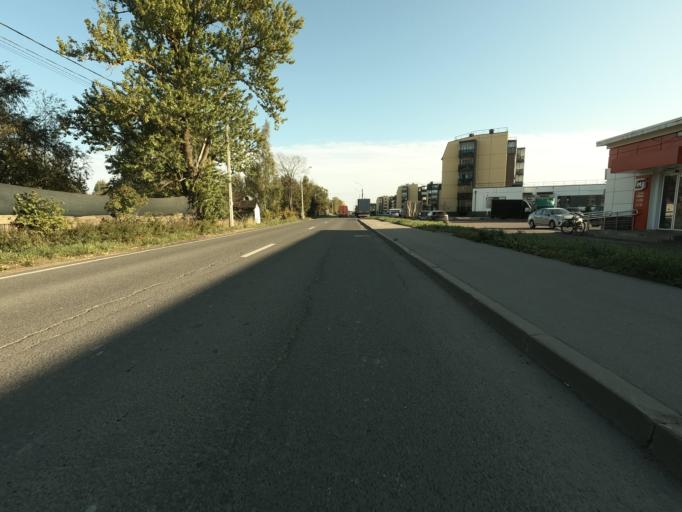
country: RU
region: St.-Petersburg
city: Pontonnyy
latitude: 59.7591
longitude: 30.6262
